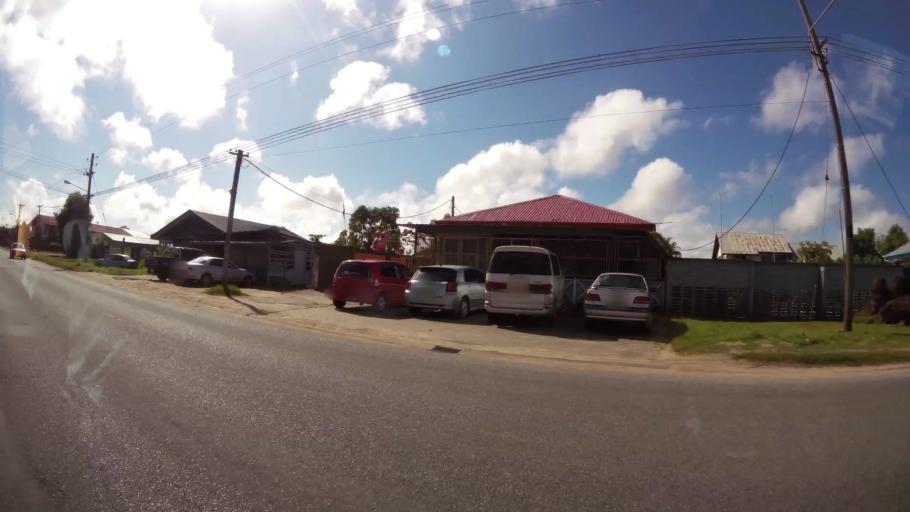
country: SR
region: Commewijne
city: Nieuw Amsterdam
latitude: 5.8415
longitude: -55.1174
